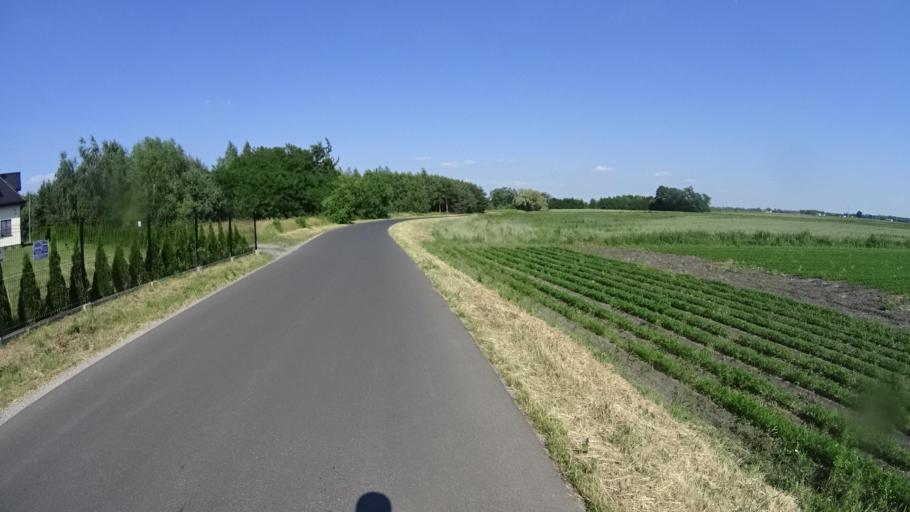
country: PL
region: Masovian Voivodeship
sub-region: Powiat warszawski zachodni
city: Blonie
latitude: 52.1636
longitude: 20.6392
